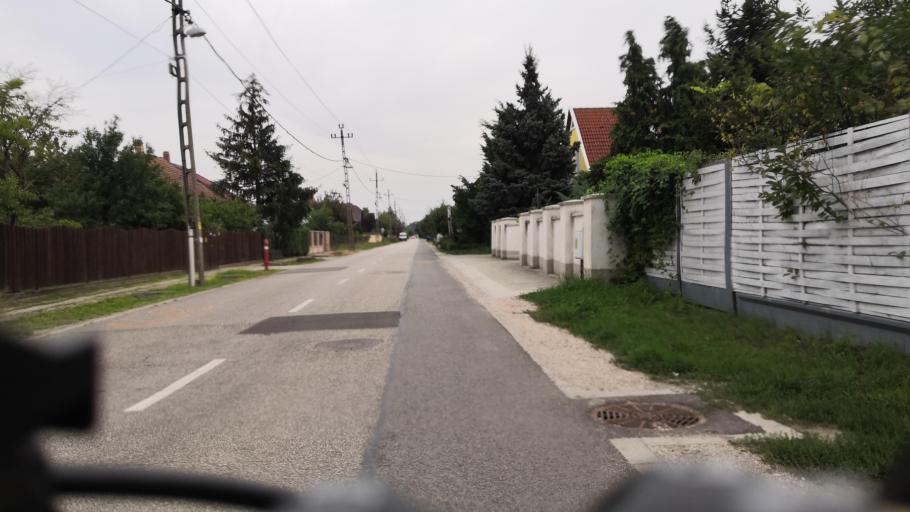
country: HU
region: Csongrad
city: Szeged
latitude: 46.2877
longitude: 20.1641
